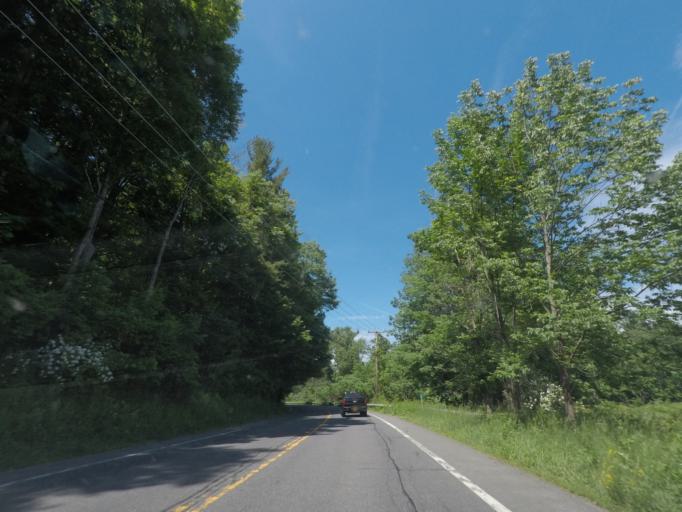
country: US
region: Massachusetts
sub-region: Berkshire County
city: Great Barrington
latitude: 42.2025
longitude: -73.5082
